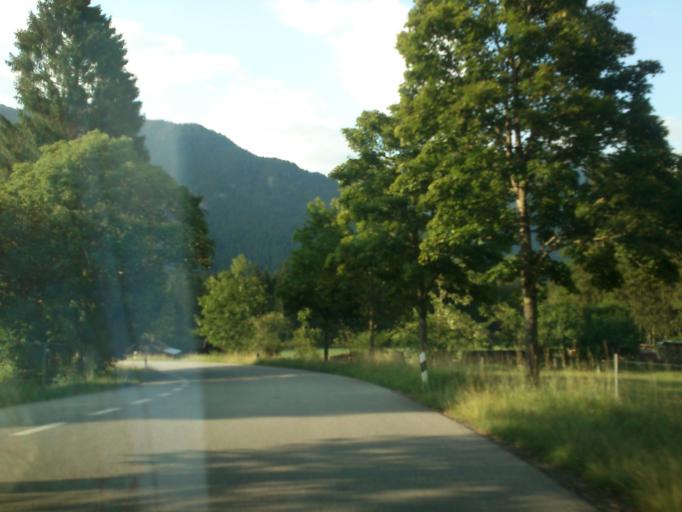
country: DE
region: Bavaria
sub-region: Upper Bavaria
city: Grainau
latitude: 47.4684
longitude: 11.0064
